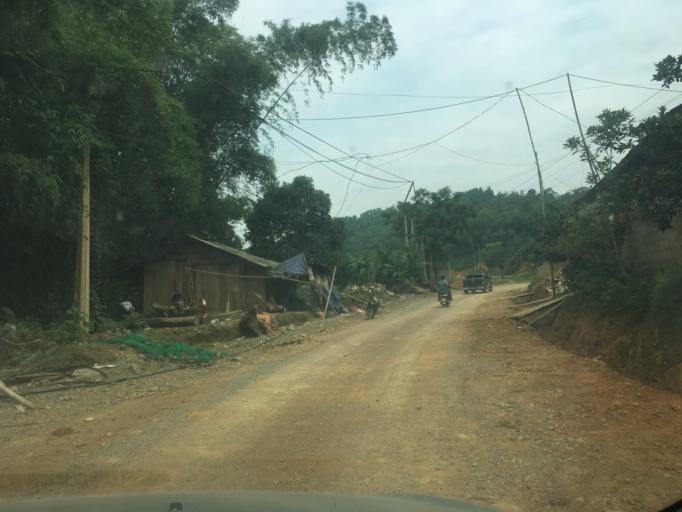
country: VN
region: Lang Son
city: Binh Gia
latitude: 22.1350
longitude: 106.3390
